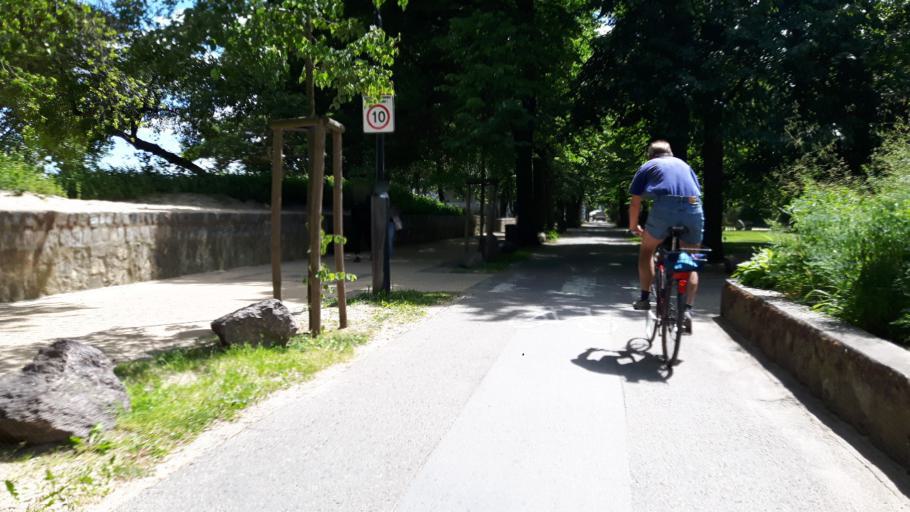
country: PL
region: Pomeranian Voivodeship
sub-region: Sopot
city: Sopot
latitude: 54.4493
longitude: 18.5673
